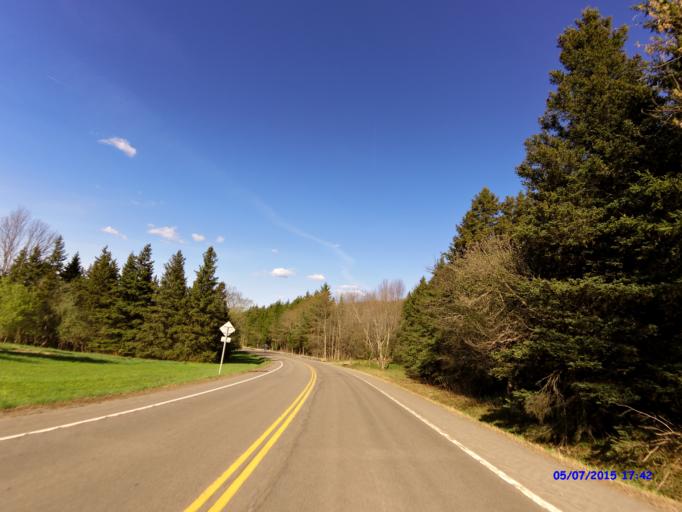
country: US
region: New York
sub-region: Cattaraugus County
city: Franklinville
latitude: 42.2980
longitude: -78.5157
